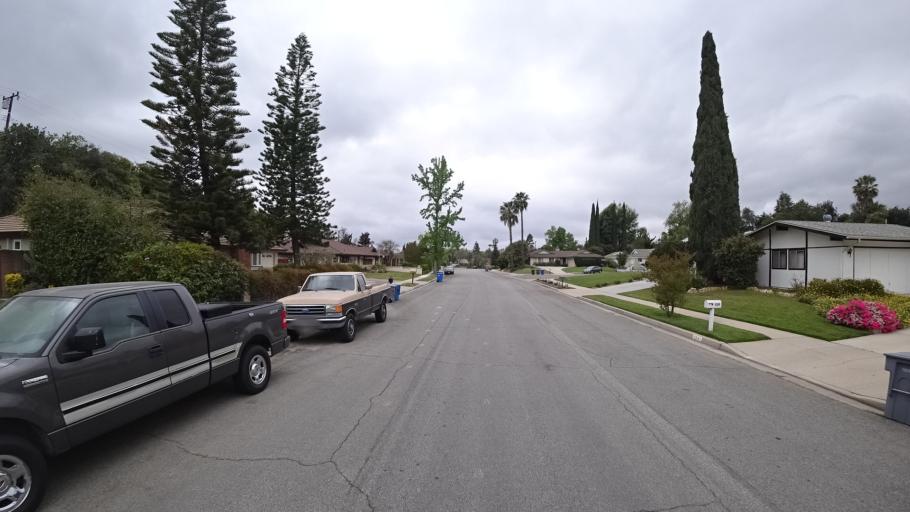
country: US
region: California
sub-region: Ventura County
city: Thousand Oaks
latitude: 34.2102
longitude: -118.8769
